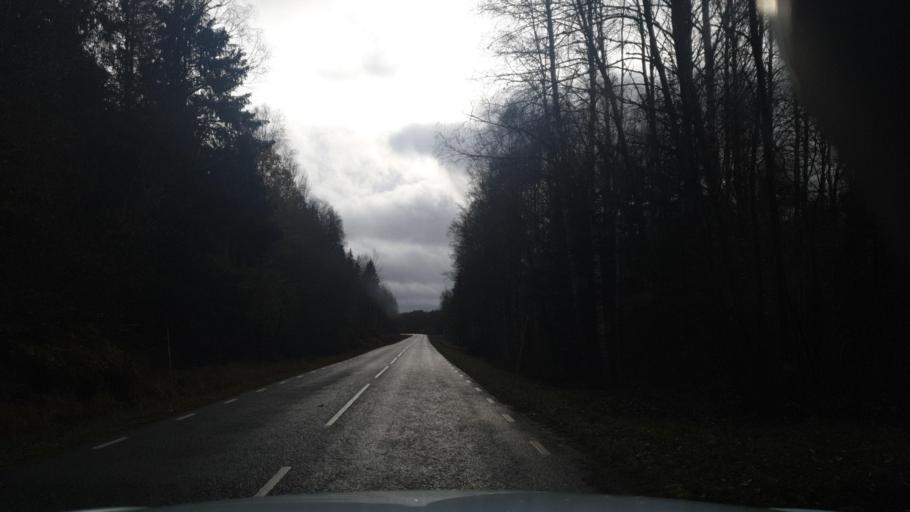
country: NO
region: Ostfold
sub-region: Romskog
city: Romskog
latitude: 59.6955
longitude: 12.0906
